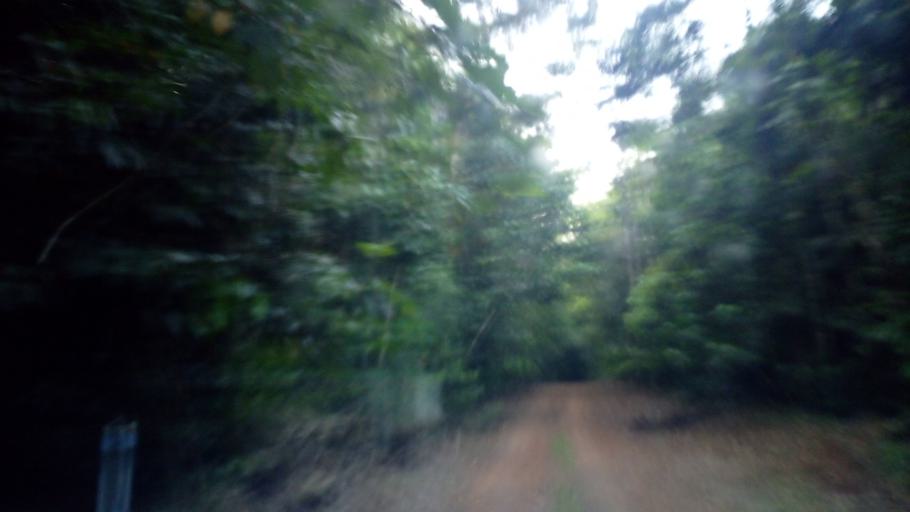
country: AU
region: Queensland
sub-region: Cassowary Coast
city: Innisfail
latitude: -17.3790
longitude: 145.7608
